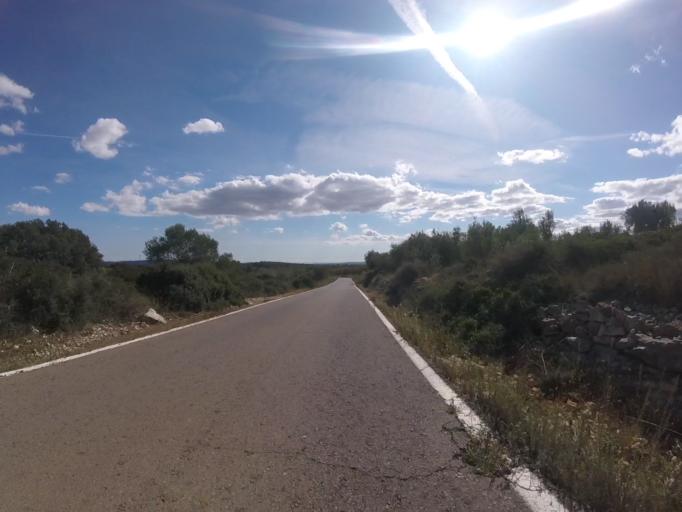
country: ES
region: Valencia
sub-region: Provincia de Castello
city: Albocasser
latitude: 40.4003
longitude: 0.0857
